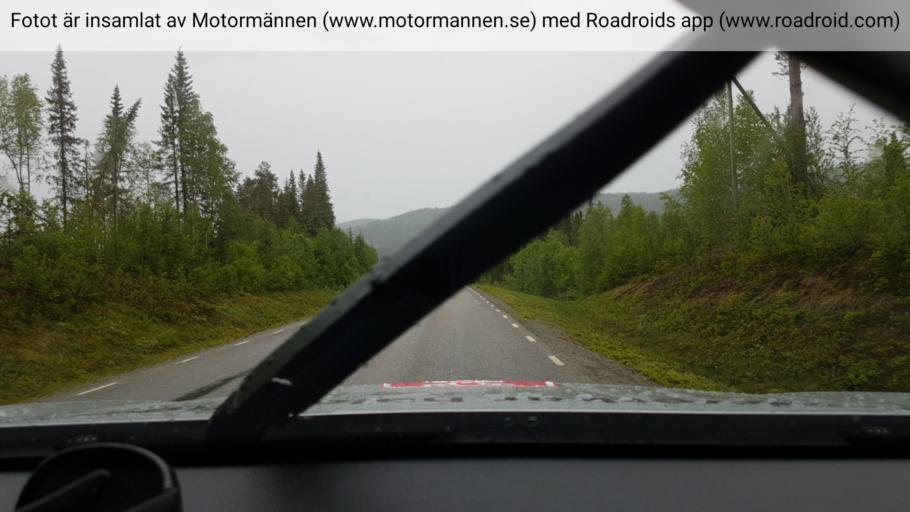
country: SE
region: Vaesterbotten
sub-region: Storumans Kommun
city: Fristad
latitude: 65.8763
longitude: 16.4071
